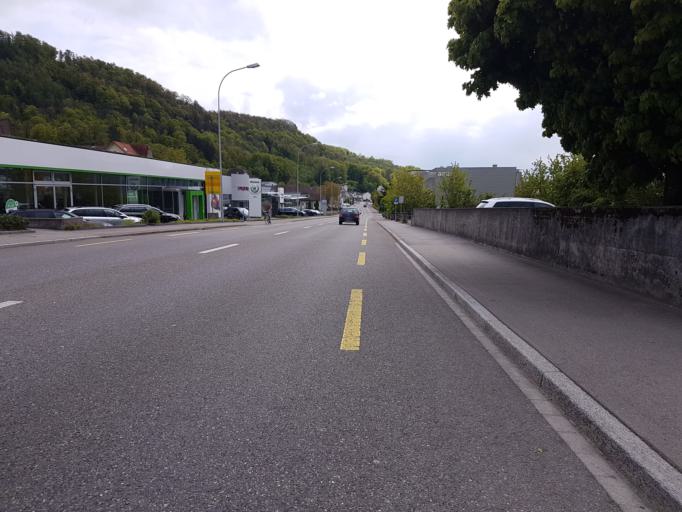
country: CH
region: Aargau
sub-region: Bezirk Brugg
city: Schinznach Bad
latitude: 47.4491
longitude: 8.1685
